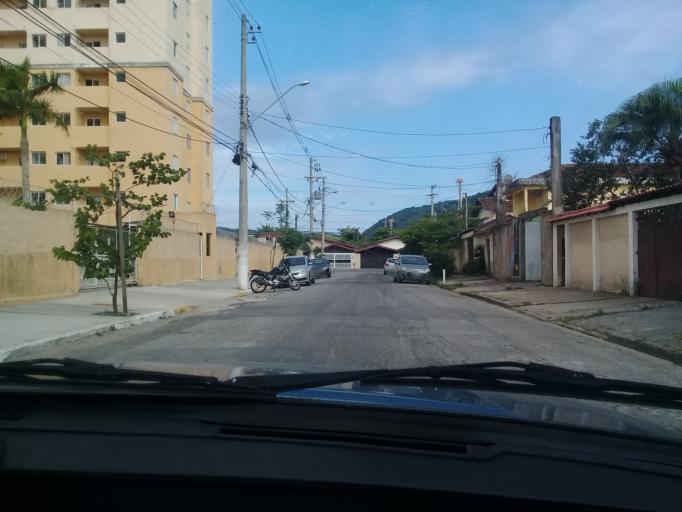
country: BR
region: Sao Paulo
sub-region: Guaruja
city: Guaruja
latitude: -23.9884
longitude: -46.2801
